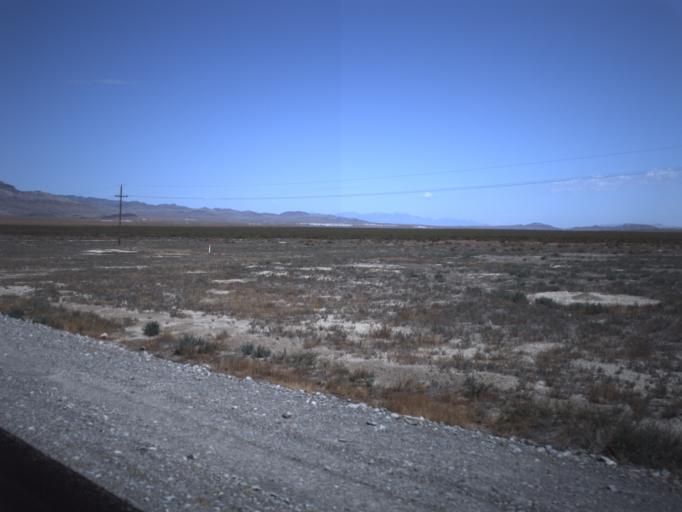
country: US
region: Utah
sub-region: Beaver County
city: Milford
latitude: 39.0750
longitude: -113.4734
